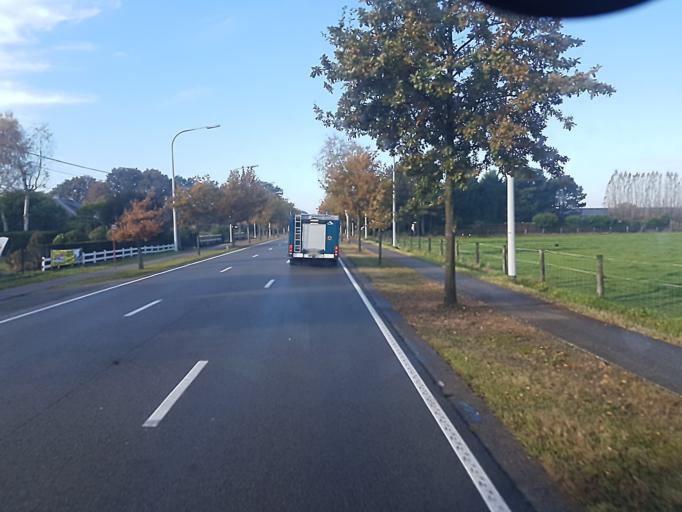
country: BE
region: Flanders
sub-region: Provincie Antwerpen
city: Oostmalle
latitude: 51.3017
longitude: 4.7705
